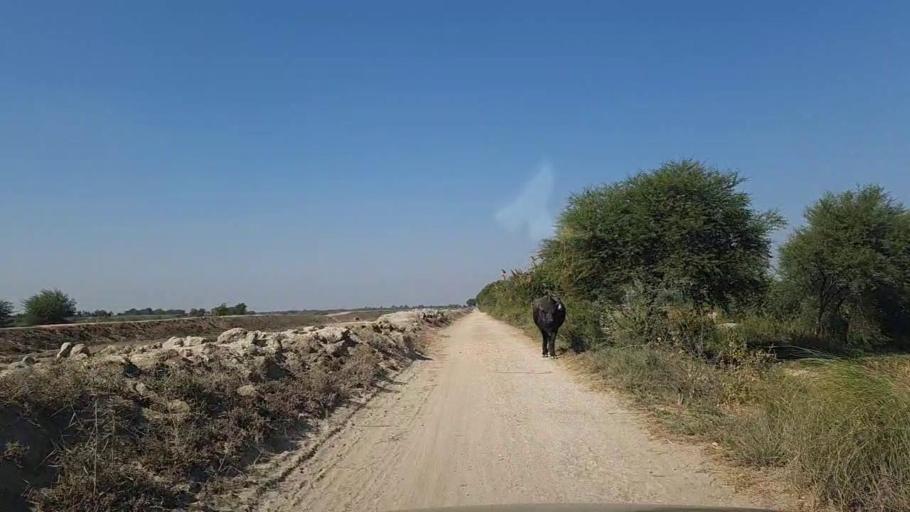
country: PK
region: Sindh
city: Mirpur Batoro
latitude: 24.7175
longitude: 68.2365
